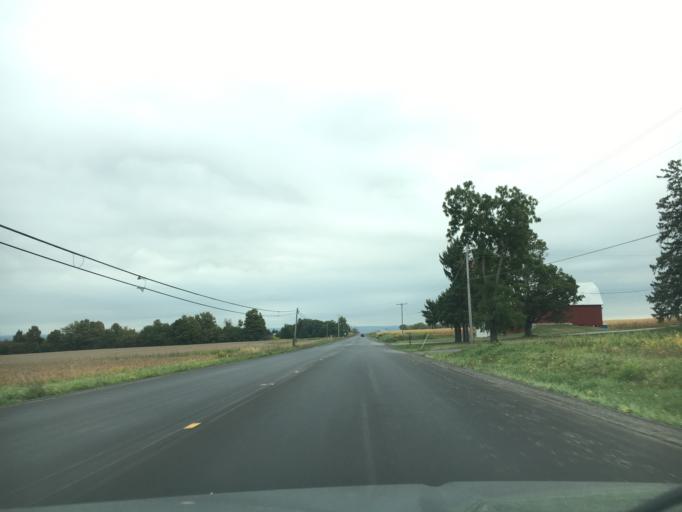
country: US
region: New York
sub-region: Cayuga County
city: Union Springs
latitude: 42.6810
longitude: -76.8109
